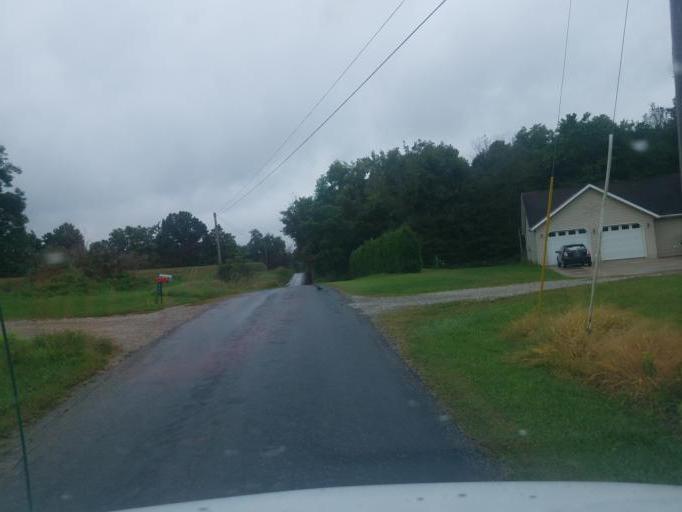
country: US
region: Ohio
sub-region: Wayne County
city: West Salem
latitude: 40.9204
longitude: -82.1527
